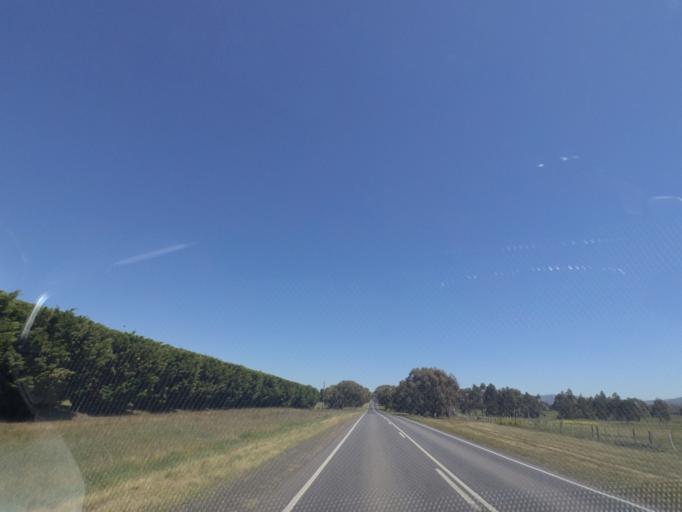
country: AU
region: Victoria
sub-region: Whittlesea
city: Whittlesea
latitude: -37.2932
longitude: 144.9252
